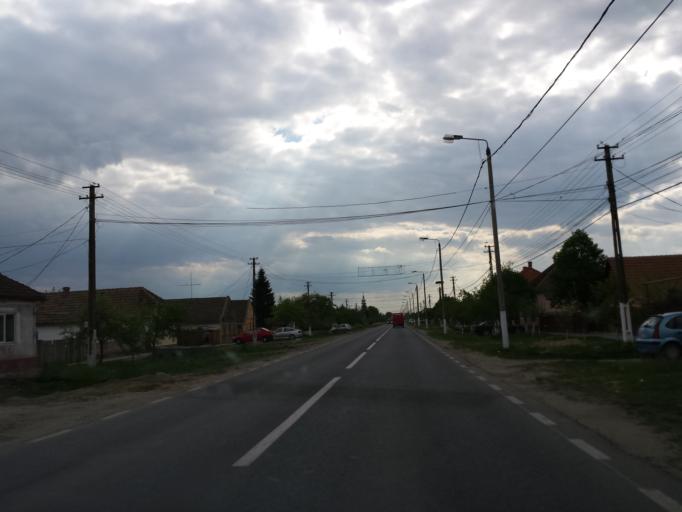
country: RO
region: Timis
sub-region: Comuna Cenad
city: Cenad
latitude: 46.1364
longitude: 20.5820
